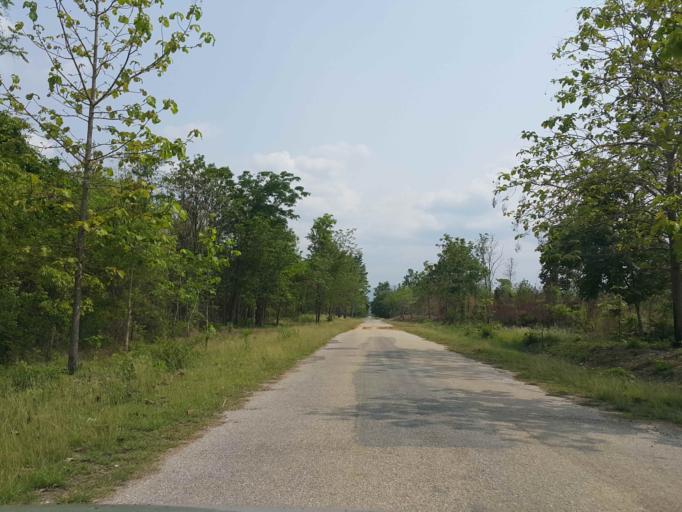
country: TH
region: Sukhothai
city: Thung Saliam
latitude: 17.3438
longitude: 99.4238
